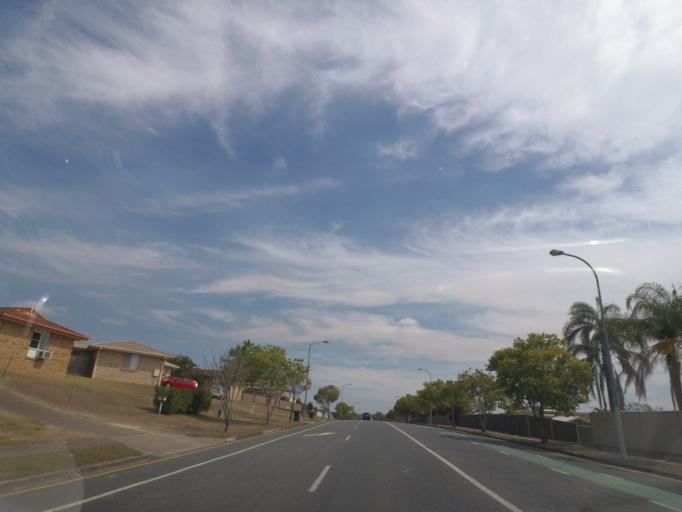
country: AU
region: Queensland
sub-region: Brisbane
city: Sunnybank Hills
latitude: -27.6187
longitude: 153.0607
